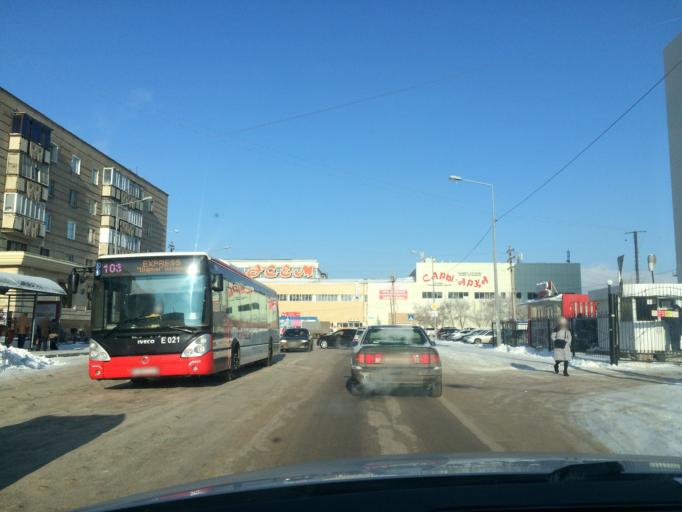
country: KZ
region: Astana Qalasy
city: Astana
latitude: 51.1800
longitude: 71.4357
